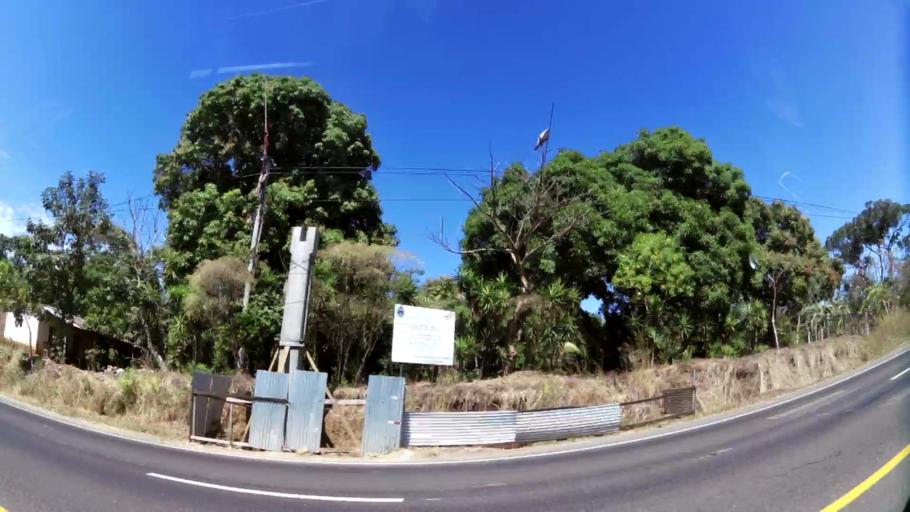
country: SV
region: Ahuachapan
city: Atiquizaya
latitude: 13.9718
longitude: -89.7315
